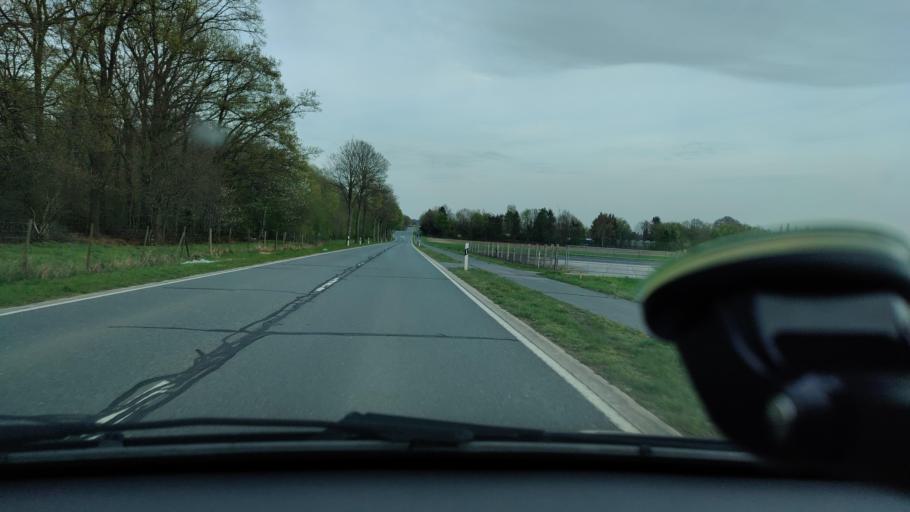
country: DE
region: North Rhine-Westphalia
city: Kalkar
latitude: 51.7428
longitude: 6.2338
